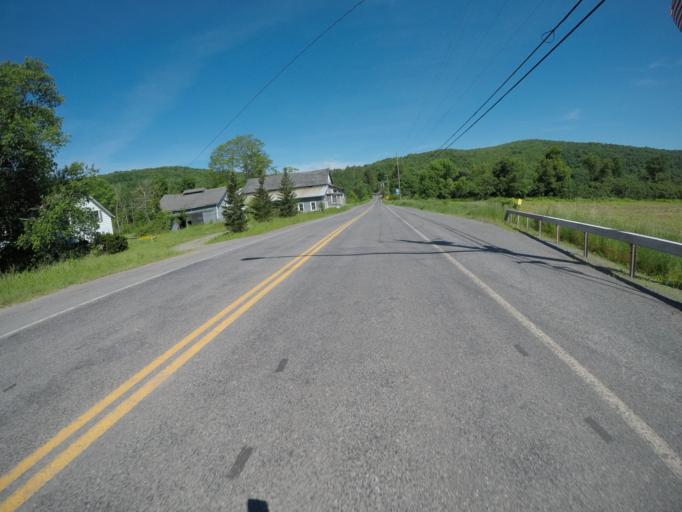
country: US
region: New York
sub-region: Delaware County
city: Delhi
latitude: 42.2090
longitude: -74.9770
